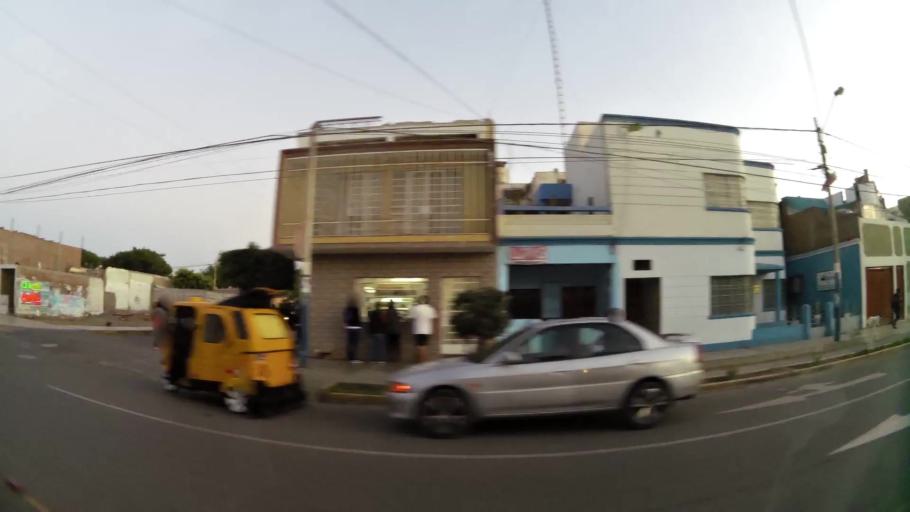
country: PE
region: Ica
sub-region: Provincia de Pisco
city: Pisco
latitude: -13.7097
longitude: -76.2088
